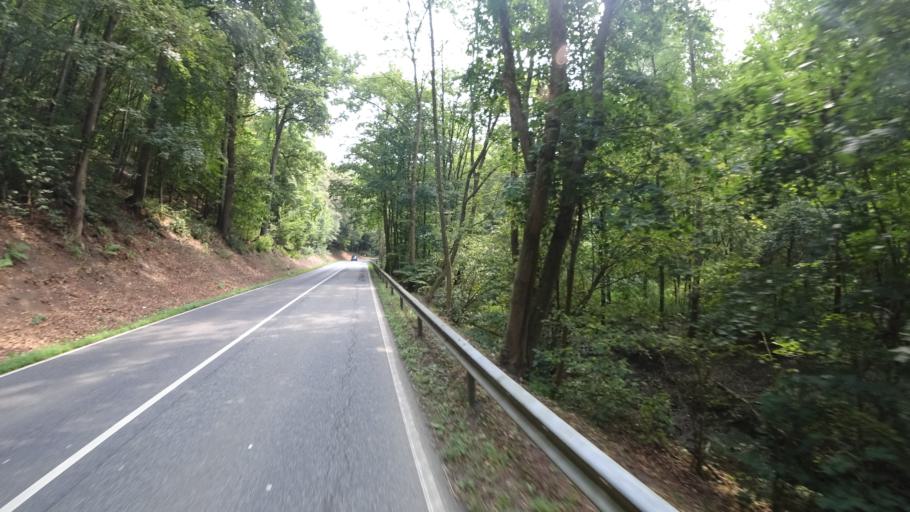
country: DE
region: Rheinland-Pfalz
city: Vallendar
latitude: 50.4170
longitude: 7.6363
